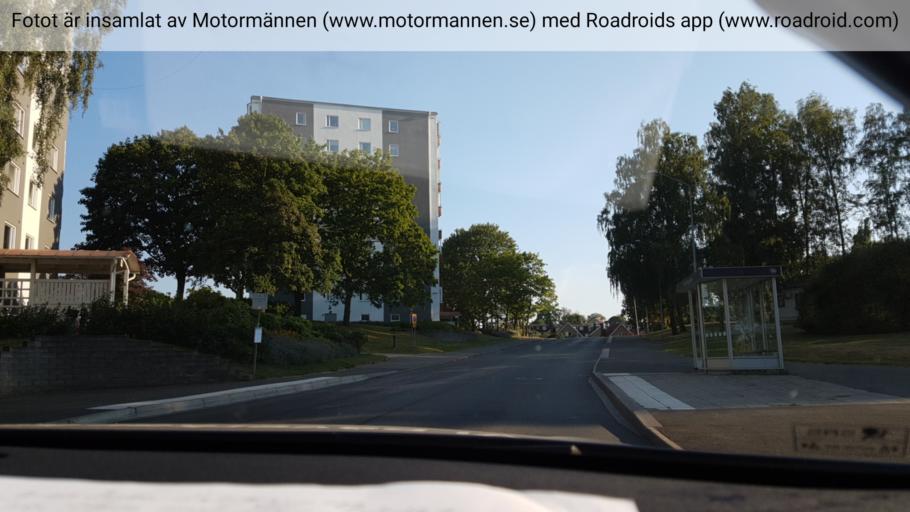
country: SE
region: Vaestra Goetaland
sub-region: Skovde Kommun
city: Skoevde
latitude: 58.3908
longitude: 13.8636
